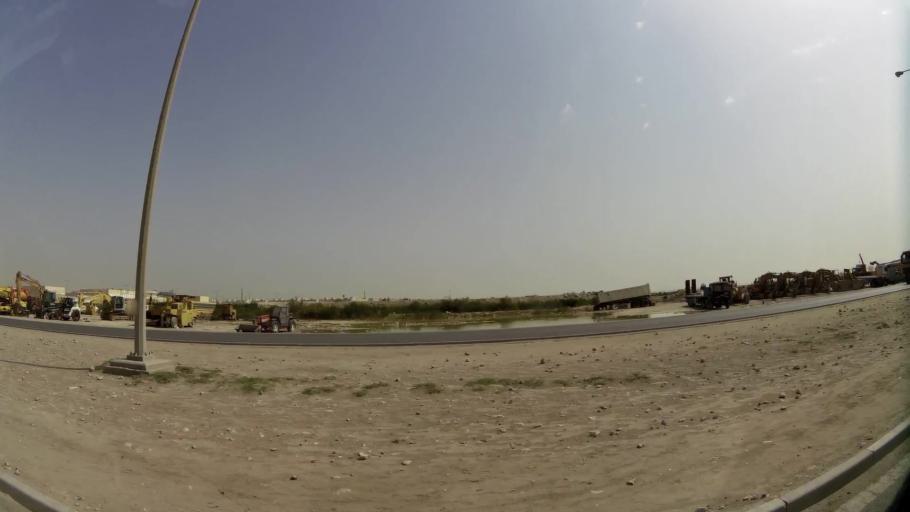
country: QA
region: Al Wakrah
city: Al Wukayr
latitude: 25.1812
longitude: 51.4631
